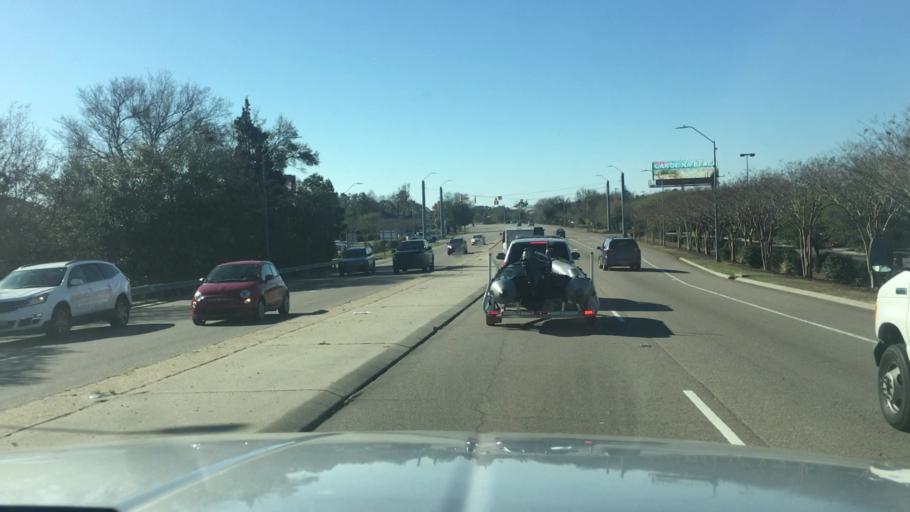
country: US
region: North Carolina
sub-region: New Hanover County
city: Sea Breeze
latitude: 34.0522
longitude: -77.8999
